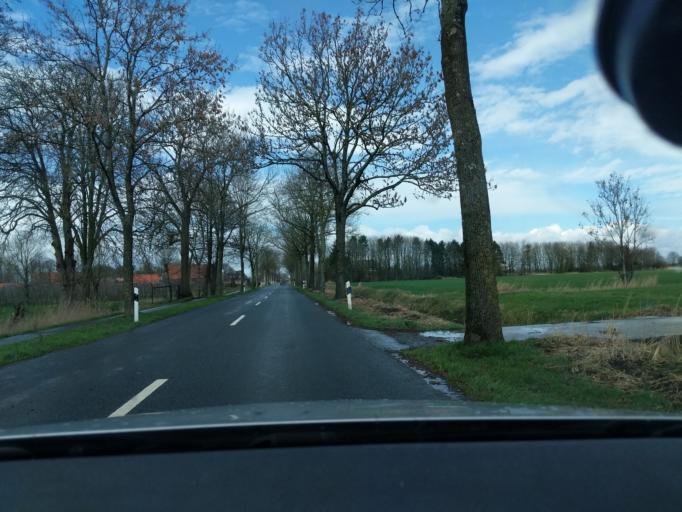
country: DE
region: Lower Saxony
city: Engelschoff
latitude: 53.6938
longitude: 9.3515
